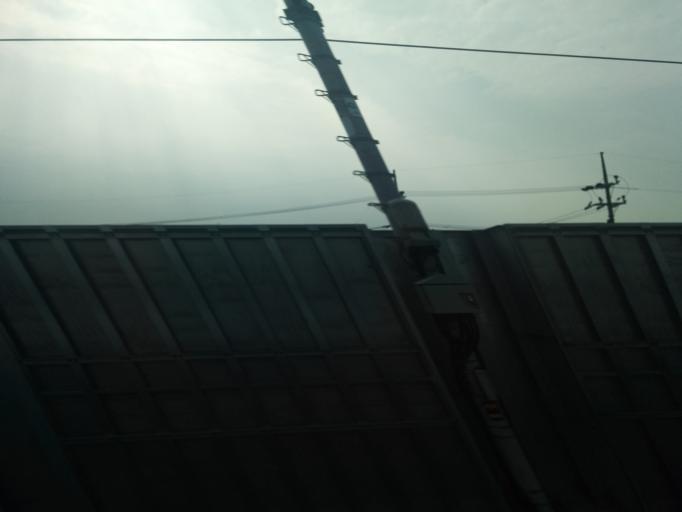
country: JP
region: Shiga Prefecture
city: Hikone
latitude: 35.1856
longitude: 136.2210
